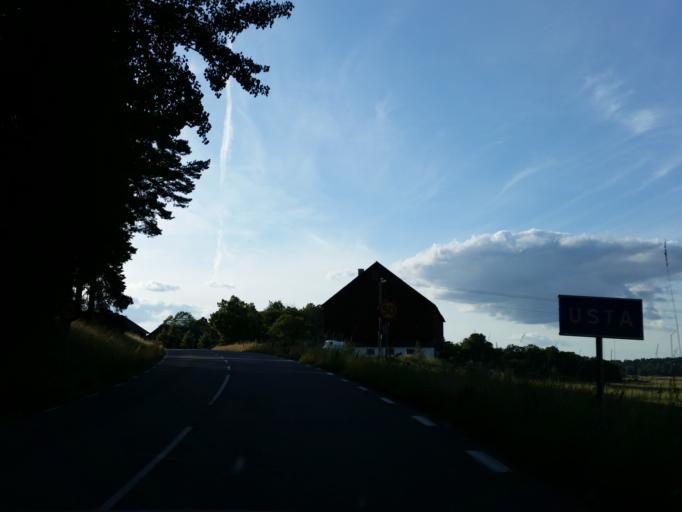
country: SE
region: Stockholm
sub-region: Sodertalje Kommun
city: Molnbo
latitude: 59.0141
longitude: 17.3697
